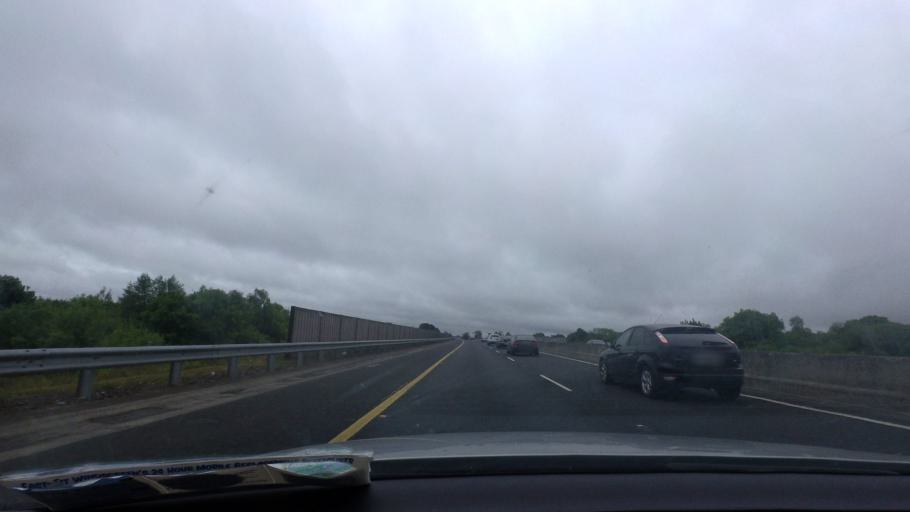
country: IE
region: Munster
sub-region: County Limerick
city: Castleconnell
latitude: 52.7128
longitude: -8.4774
